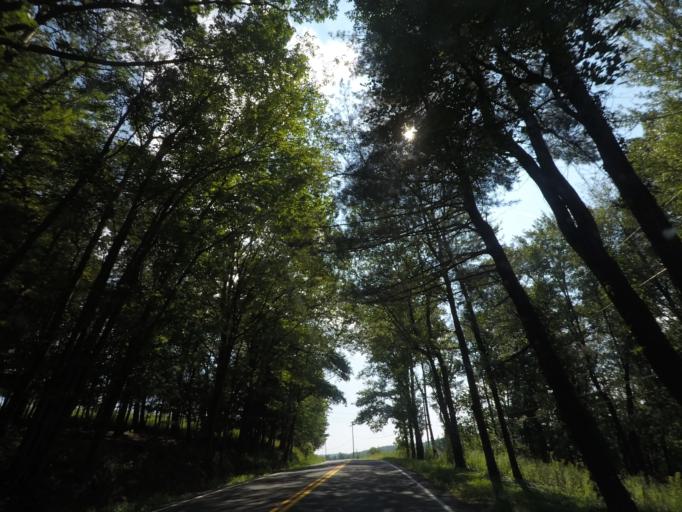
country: US
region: New York
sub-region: Rensselaer County
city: Poestenkill
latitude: 42.7942
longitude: -73.5309
